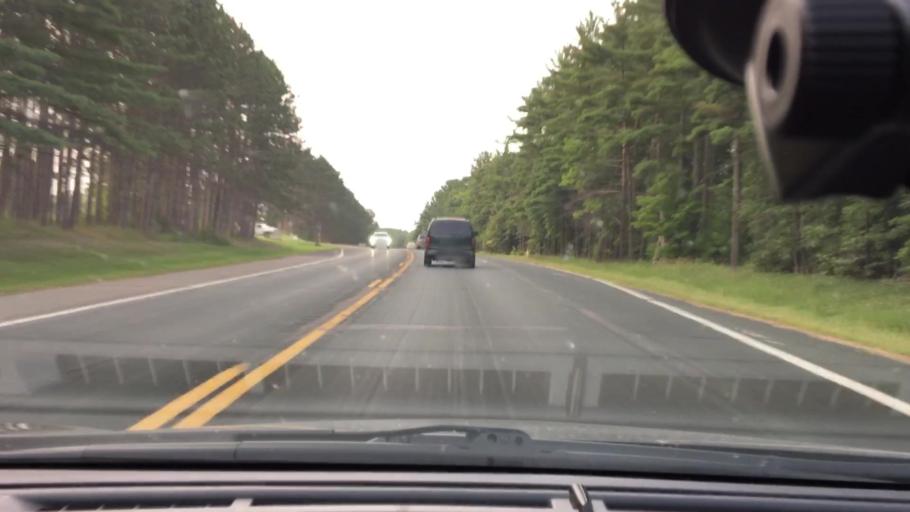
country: US
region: Minnesota
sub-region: Mille Lacs County
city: Vineland
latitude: 46.2241
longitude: -93.7919
